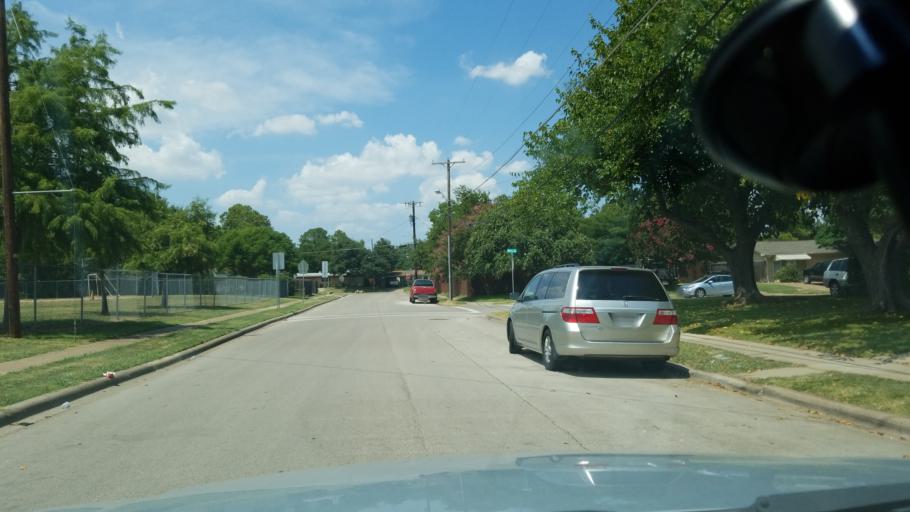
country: US
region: Texas
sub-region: Dallas County
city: Irving
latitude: 32.8229
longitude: -96.9852
